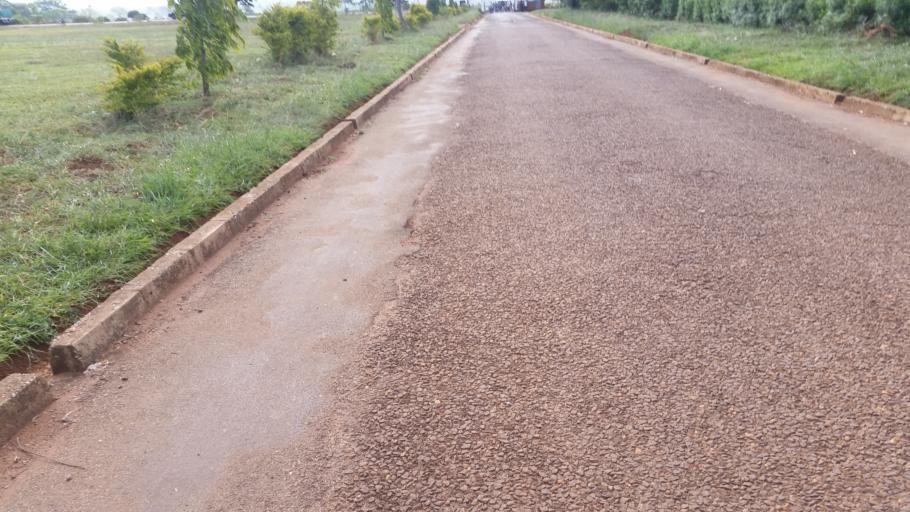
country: UG
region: Eastern Region
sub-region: Busia District
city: Busia
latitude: 0.5492
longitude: 34.0207
